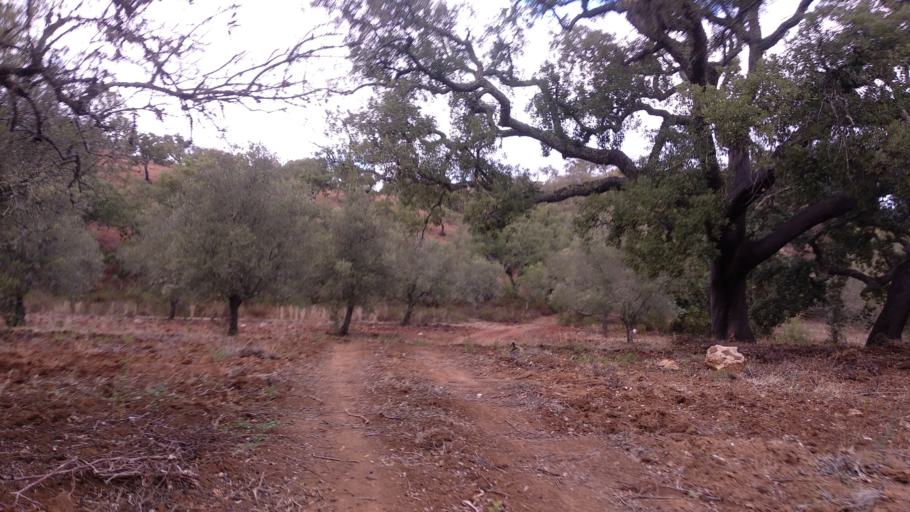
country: PT
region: Faro
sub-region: Sao Bras de Alportel
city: Sao Bras de Alportel
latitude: 37.1611
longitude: -7.9075
